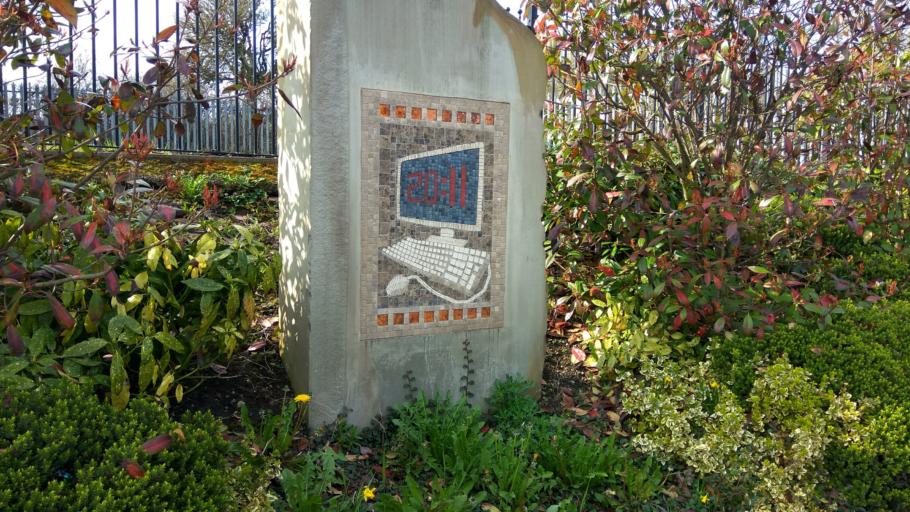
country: GB
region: England
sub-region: City and Borough of Leeds
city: Morley
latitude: 53.7217
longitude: -1.5901
